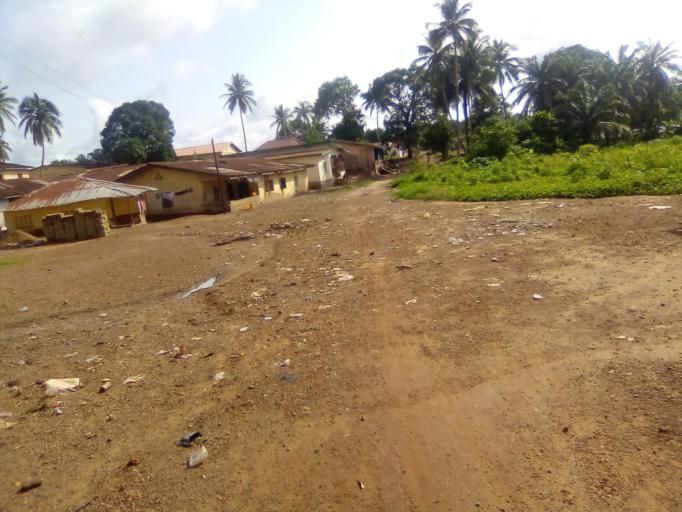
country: SL
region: Southern Province
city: Bo
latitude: 7.9733
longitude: -11.7297
